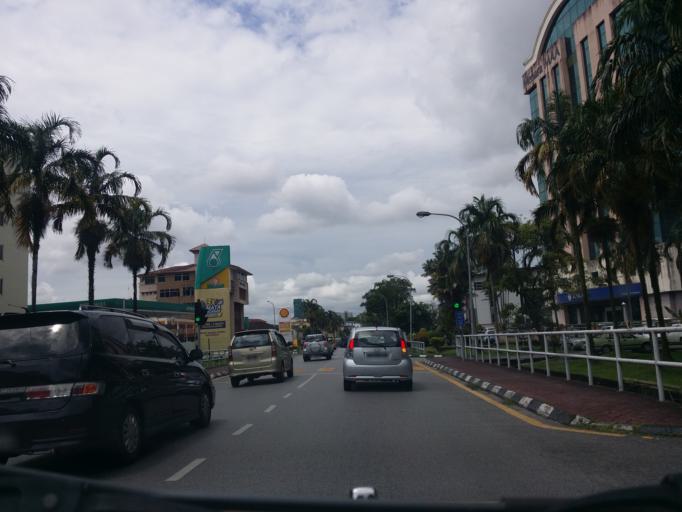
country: MY
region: Sarawak
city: Kuching
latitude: 1.5527
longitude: 110.3560
